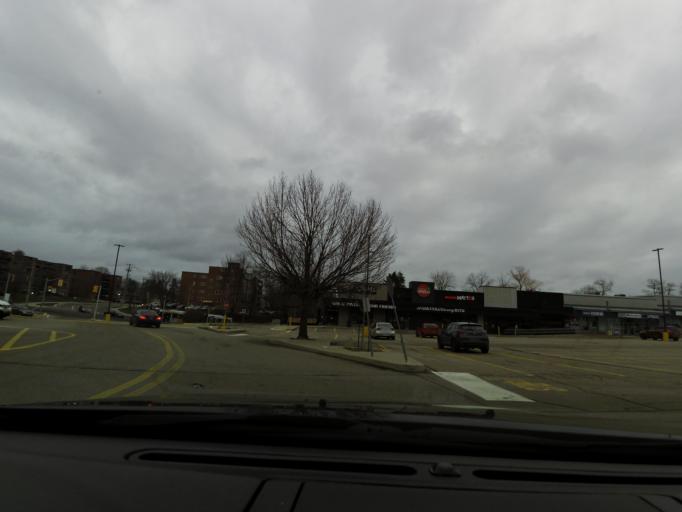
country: CA
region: Ontario
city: Ancaster
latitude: 43.2584
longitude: -79.9423
